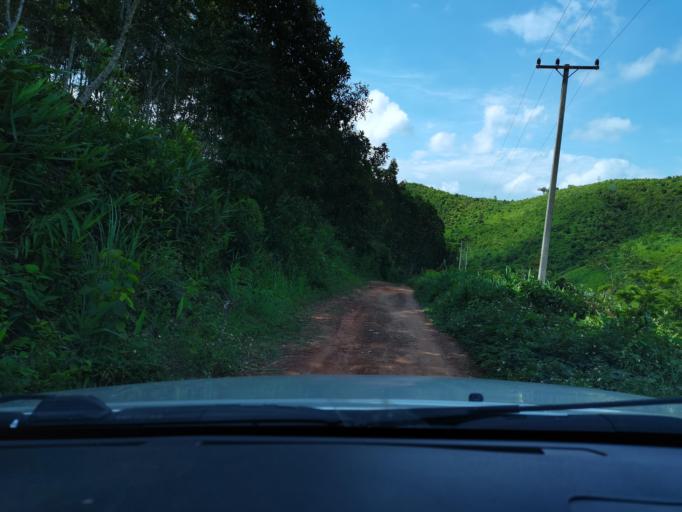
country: LA
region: Loungnamtha
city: Muang Nale
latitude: 20.5662
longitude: 101.0574
